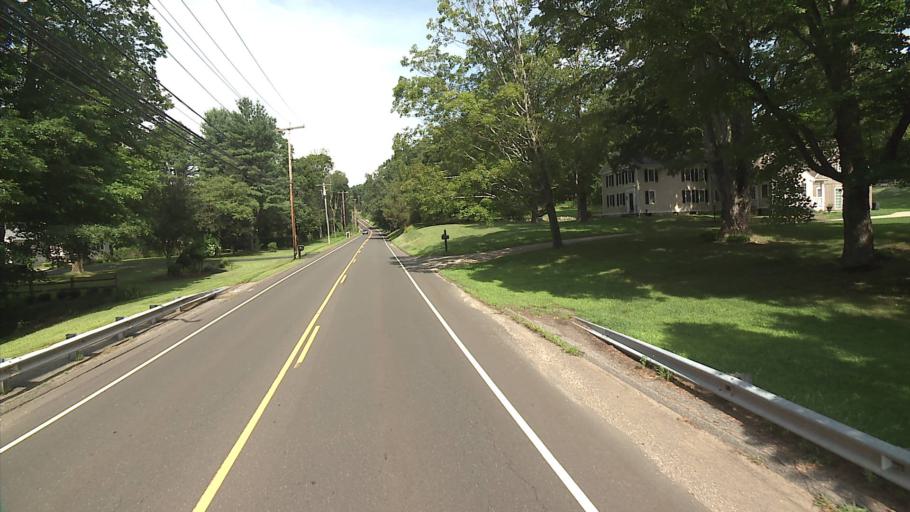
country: US
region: Connecticut
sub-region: New Haven County
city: Woodbridge
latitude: 41.3298
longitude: -73.0298
